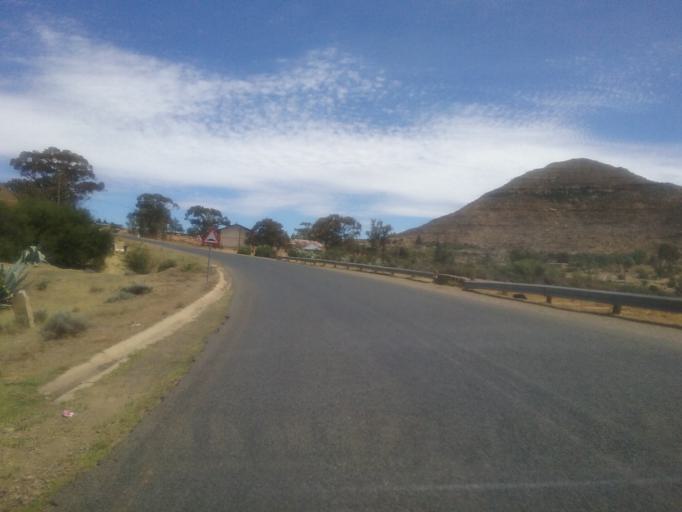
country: LS
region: Mafeteng
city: Mafeteng
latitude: -29.9544
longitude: 27.2866
